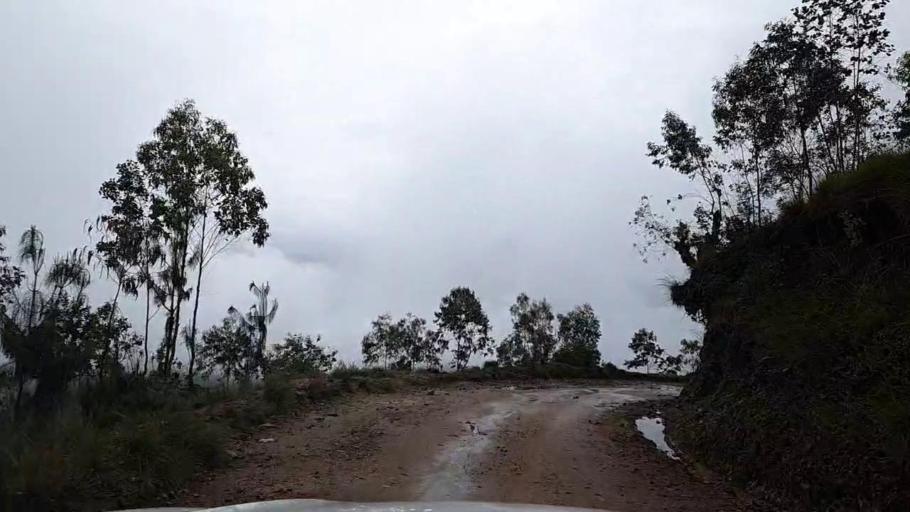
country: RW
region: Southern Province
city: Nzega
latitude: -2.4086
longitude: 29.4909
